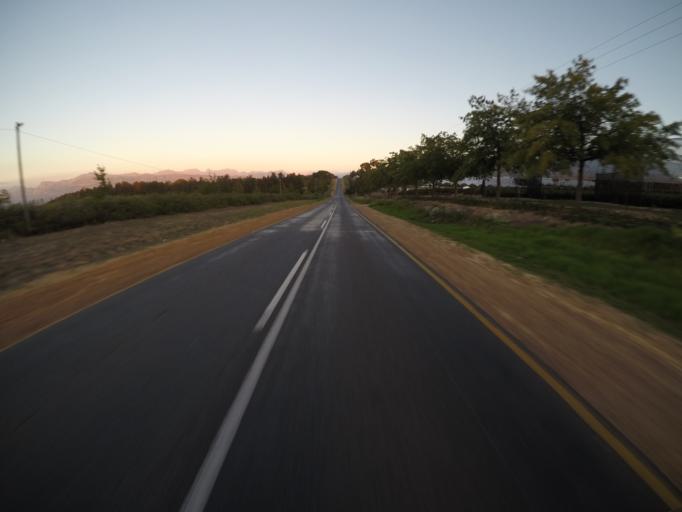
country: ZA
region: Western Cape
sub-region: Cape Winelands District Municipality
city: Paarl
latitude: -33.8070
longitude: 18.9000
